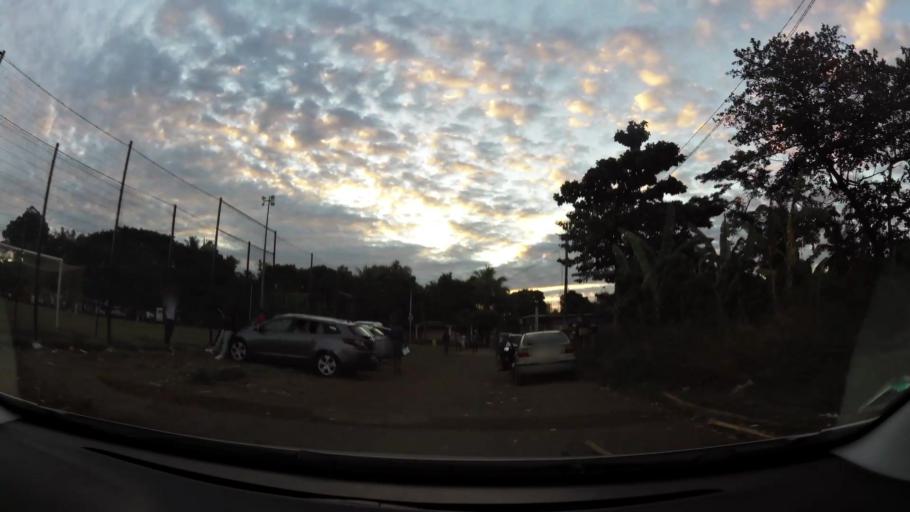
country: YT
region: Koungou
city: Koungou
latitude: -12.7345
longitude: 45.1618
